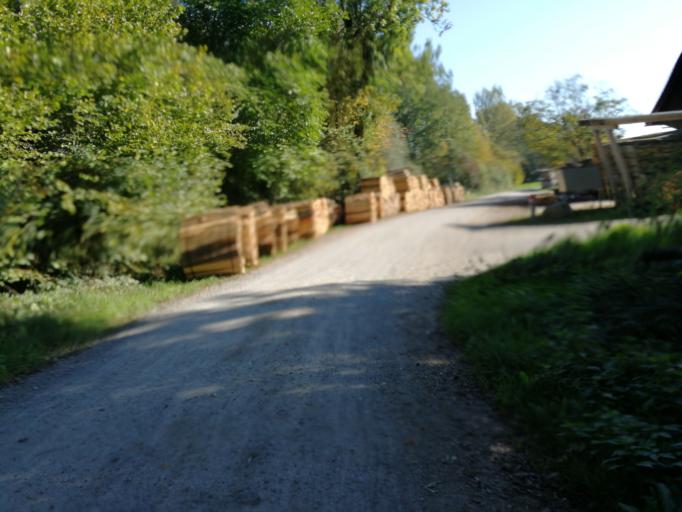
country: CH
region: Zurich
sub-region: Bezirk Uster
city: Monchaltorf
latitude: 47.3196
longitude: 8.7110
